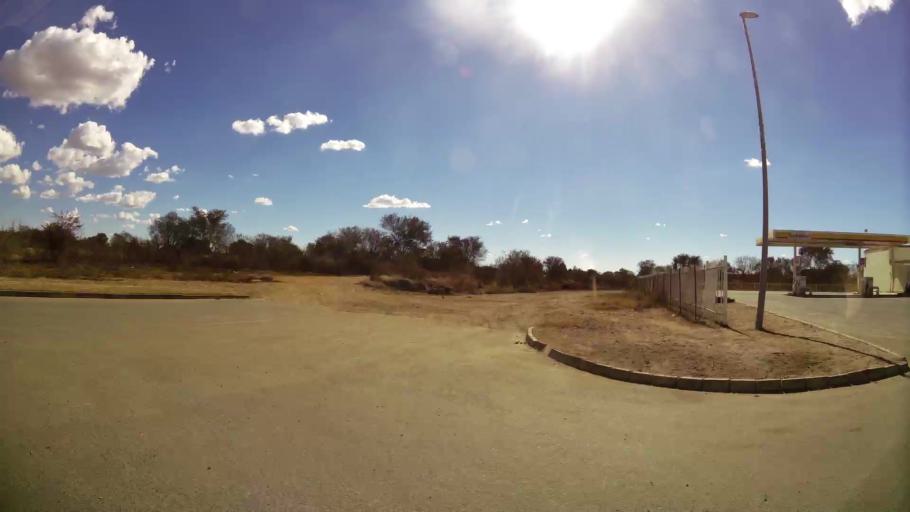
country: ZA
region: North-West
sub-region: Dr Kenneth Kaunda District Municipality
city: Klerksdorp
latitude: -26.8677
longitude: 26.6271
